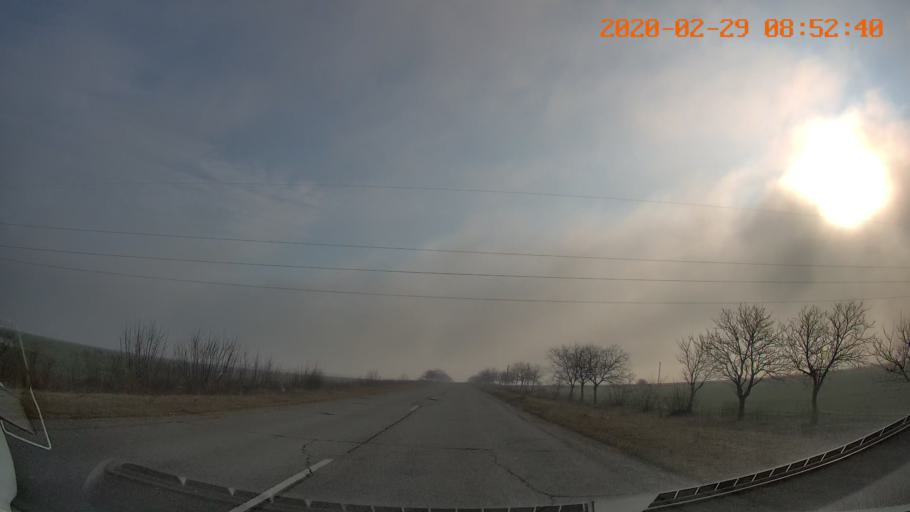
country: MD
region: Anenii Noi
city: Varnita
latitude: 46.9241
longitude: 29.5422
